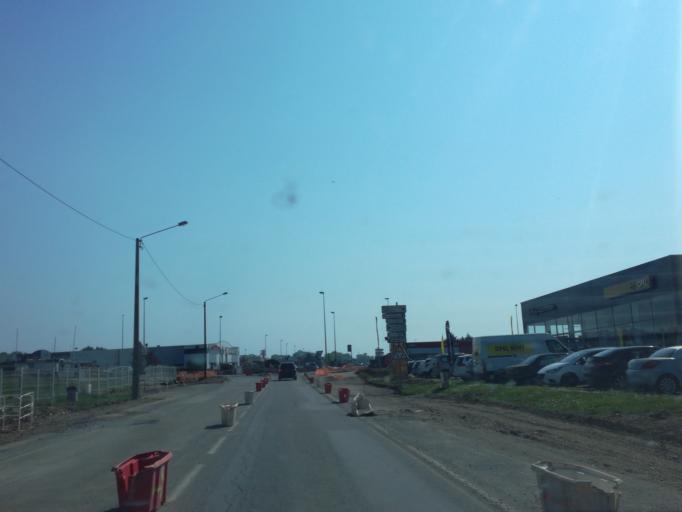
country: FR
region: Brittany
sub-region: Departement du Morbihan
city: Le Sourn
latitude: 48.0418
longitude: -2.9608
